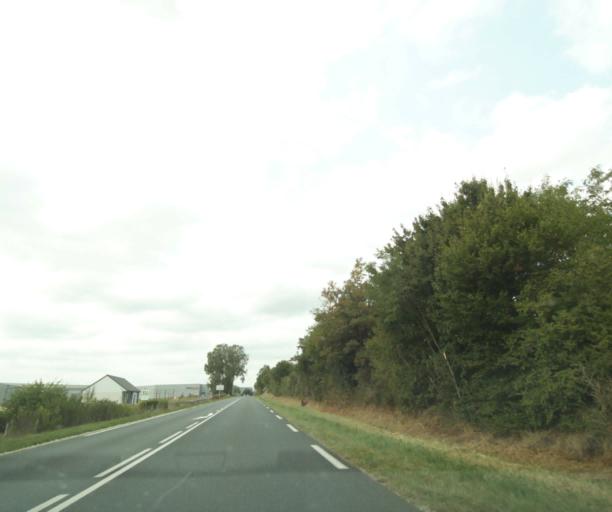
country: FR
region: Centre
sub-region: Departement de l'Indre
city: Buzancais
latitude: 46.8869
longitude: 1.4055
